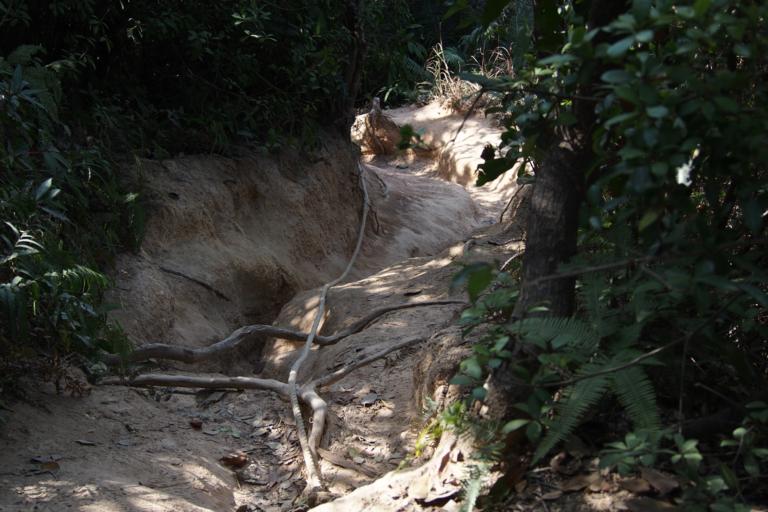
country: CN
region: Guangdong
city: Shahe
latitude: 22.5828
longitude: 114.0112
